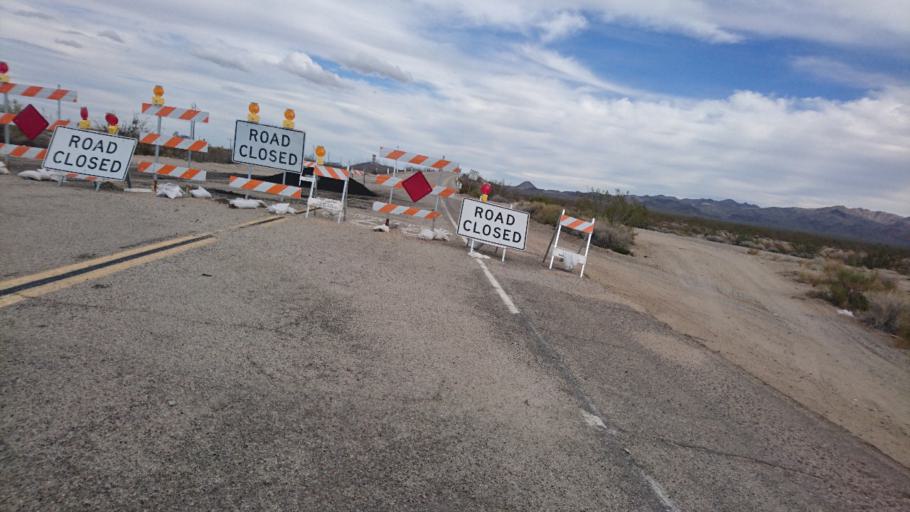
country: US
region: California
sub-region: San Bernardino County
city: Needles
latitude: 34.7525
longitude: -115.2248
